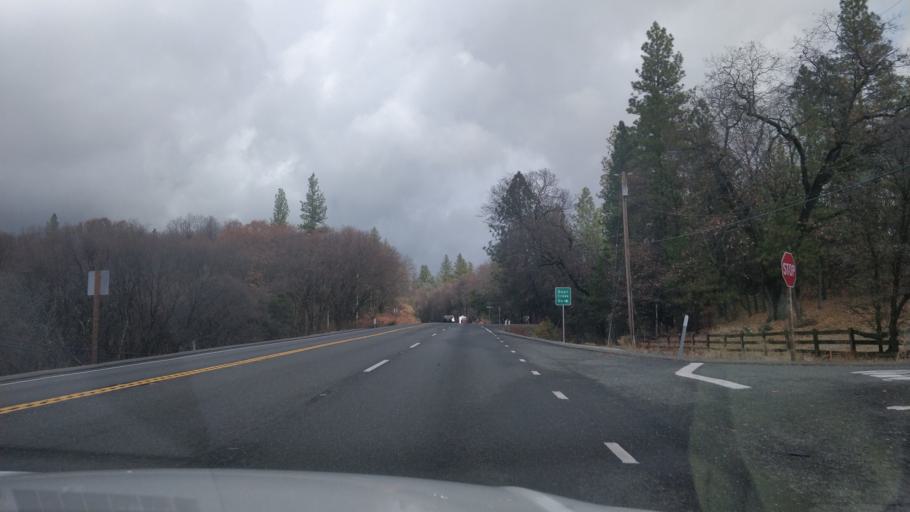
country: US
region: California
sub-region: Nevada County
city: Alta Sierra
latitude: 39.1304
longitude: -121.0744
